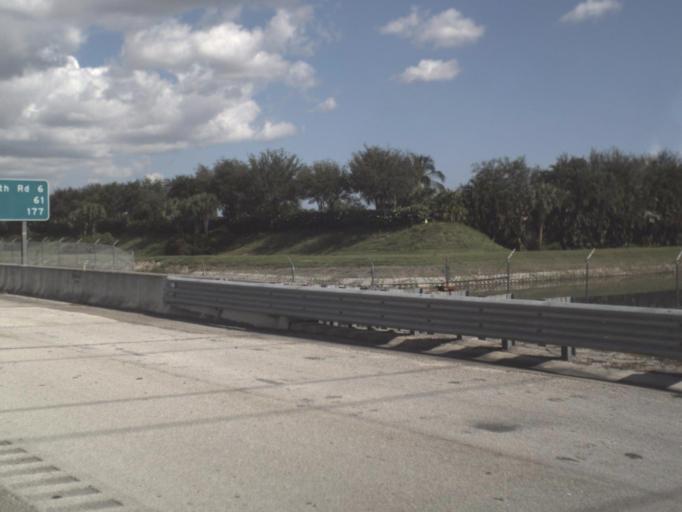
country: US
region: Florida
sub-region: Palm Beach County
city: Villages of Oriole
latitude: 26.5387
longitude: -80.1726
